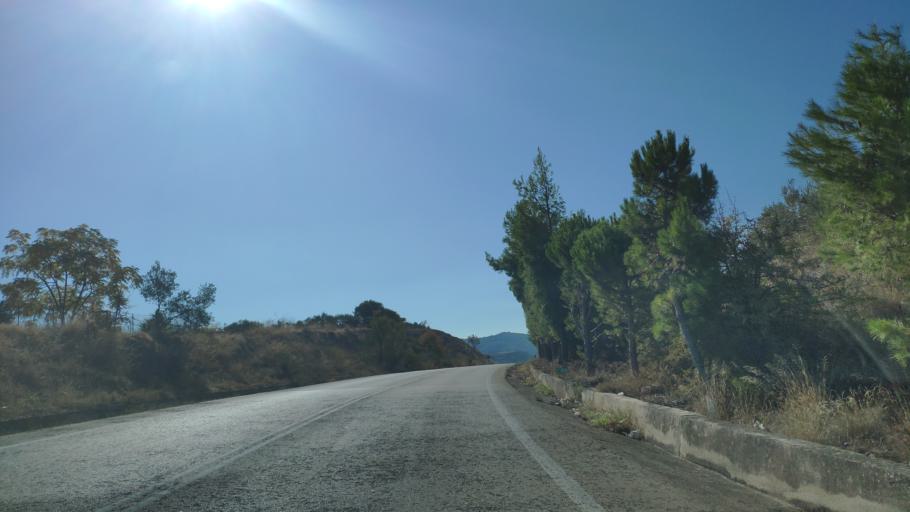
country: GR
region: Peloponnese
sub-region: Nomos Korinthias
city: Arkhaia Korinthos
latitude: 37.9121
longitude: 22.8979
